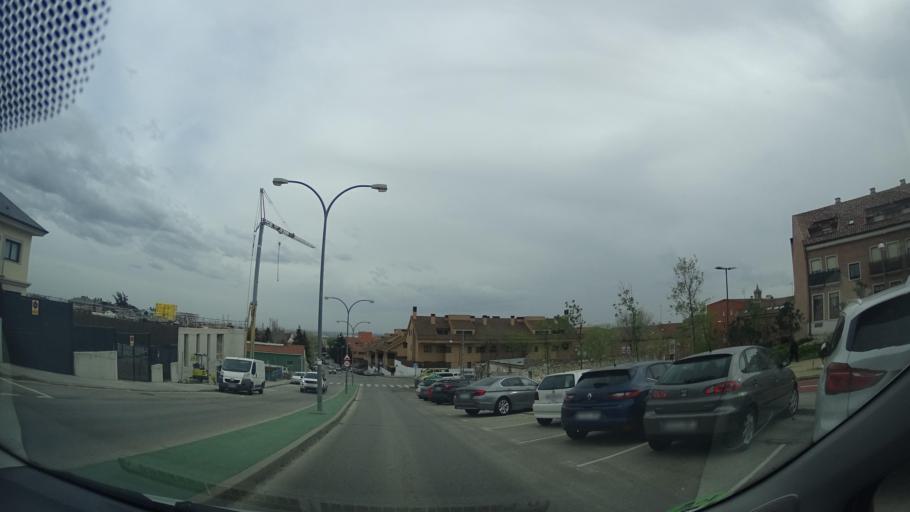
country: ES
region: Madrid
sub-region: Provincia de Madrid
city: Colmenar Viejo
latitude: 40.6626
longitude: -3.7635
